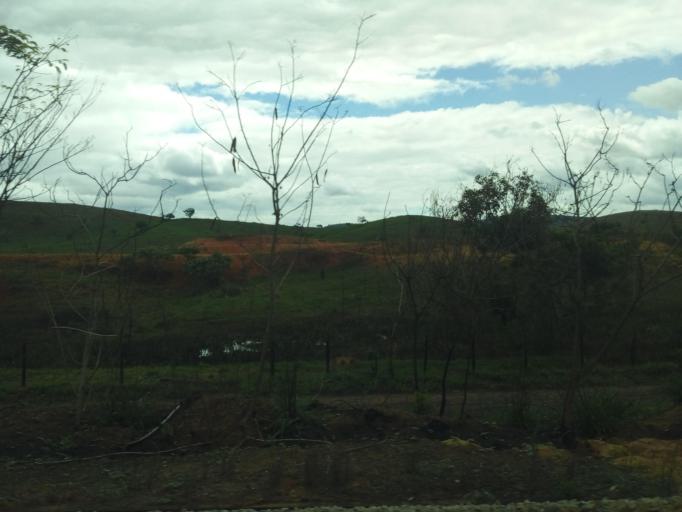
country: BR
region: Minas Gerais
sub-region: Governador Valadares
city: Governador Valadares
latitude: -19.0617
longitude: -42.1486
